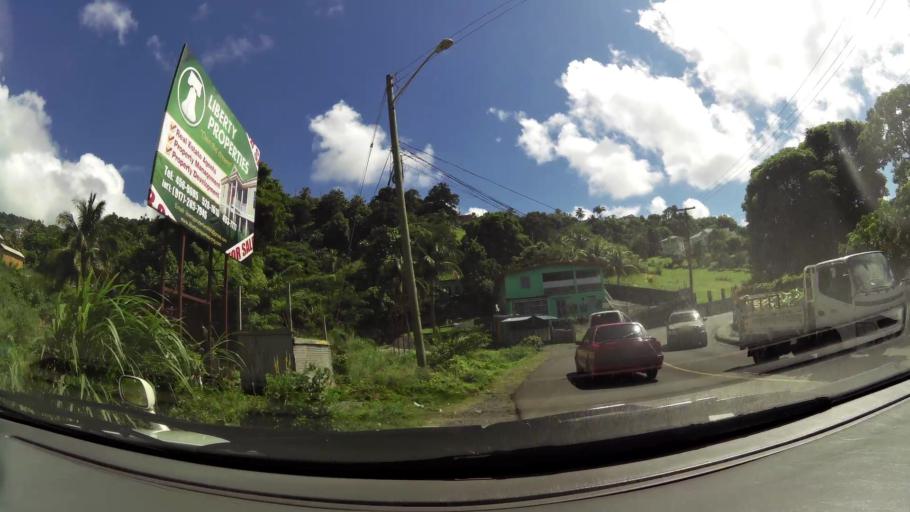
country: VC
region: Saint George
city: Kingstown
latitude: 13.1575
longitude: -61.2209
